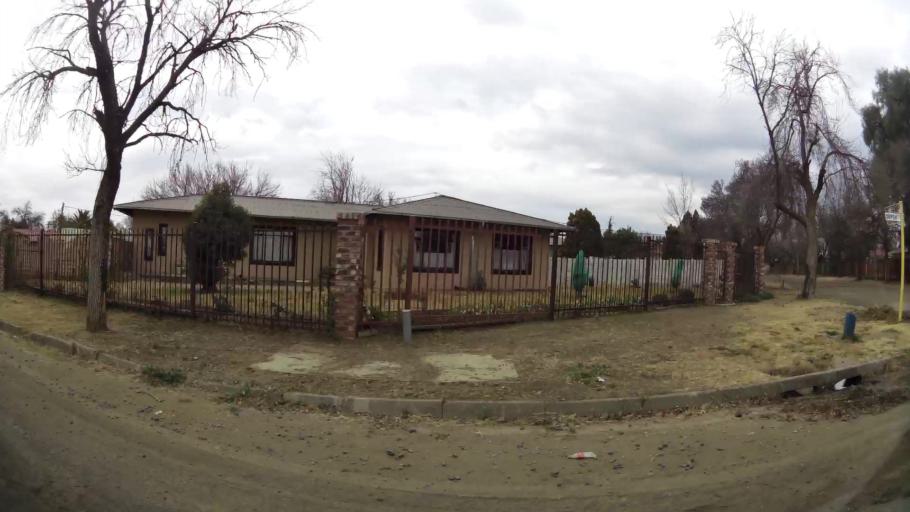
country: ZA
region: Orange Free State
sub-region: Fezile Dabi District Municipality
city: Kroonstad
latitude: -27.6767
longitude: 27.2323
